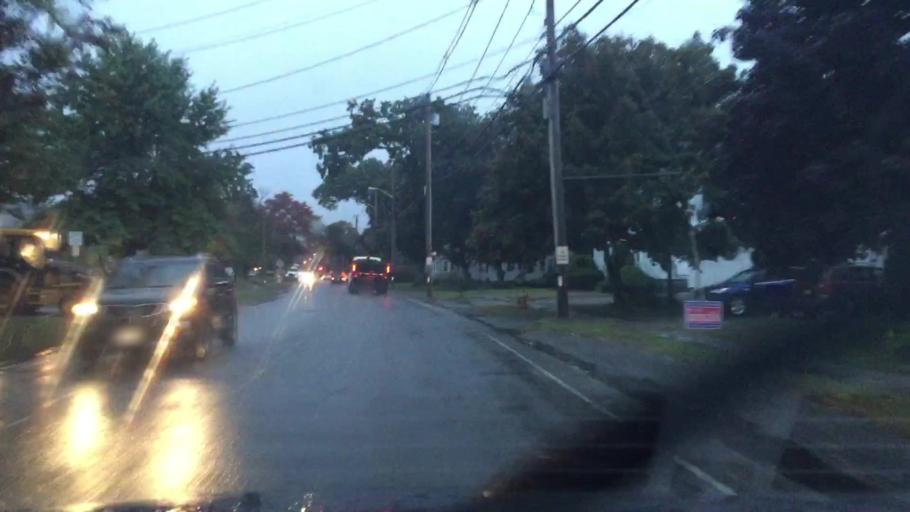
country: US
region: Massachusetts
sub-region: Essex County
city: North Andover
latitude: 42.6987
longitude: -71.1350
